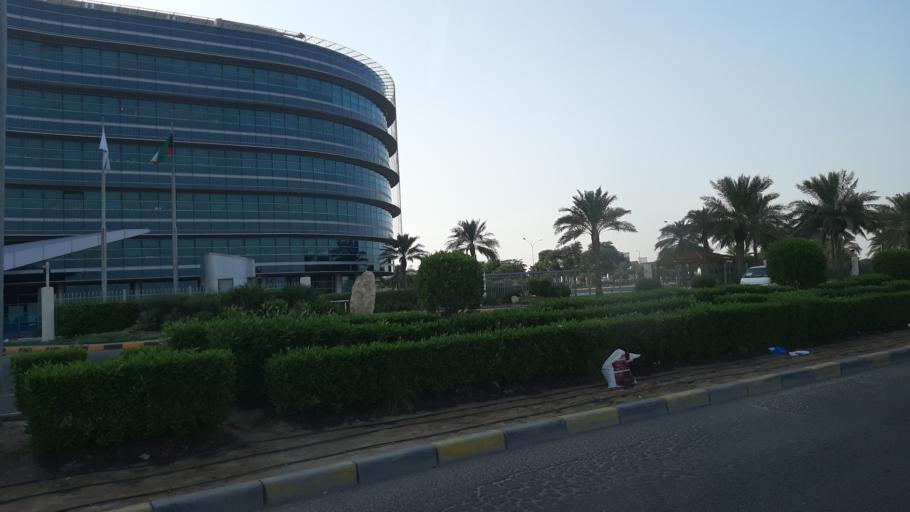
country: KW
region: Al Ahmadi
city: Al Ahmadi
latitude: 29.0932
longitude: 48.0883
